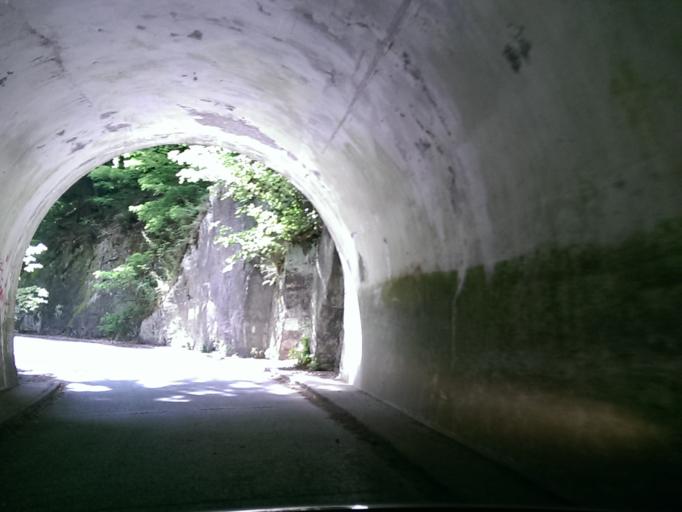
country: CZ
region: Central Bohemia
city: Mseno
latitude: 50.4397
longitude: 14.5754
